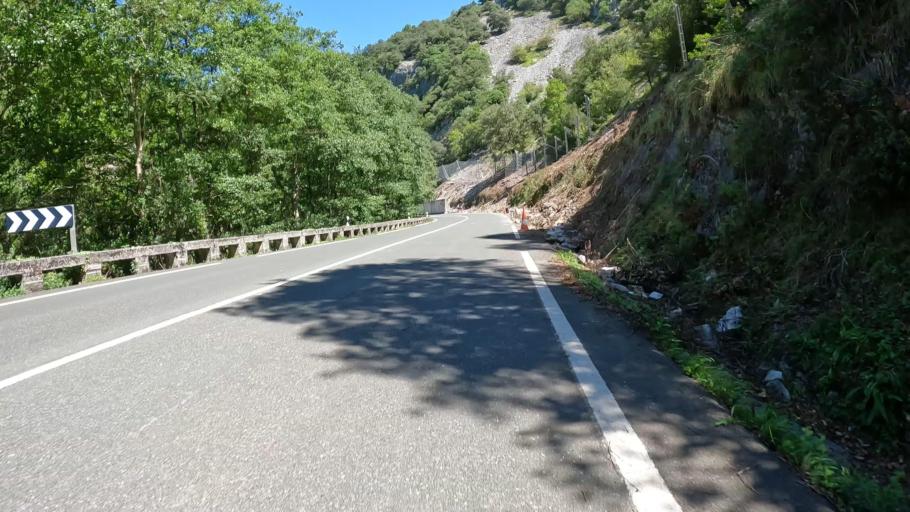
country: ES
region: Basque Country
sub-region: Provincia de Guipuzcoa
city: Oreja
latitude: 43.0778
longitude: -2.0175
